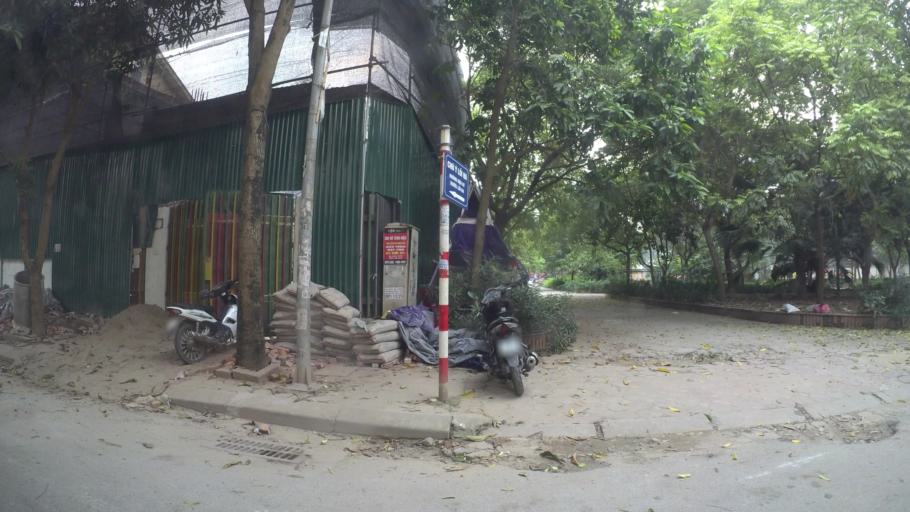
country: VN
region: Ha Noi
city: Cau Dien
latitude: 21.0321
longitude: 105.7638
